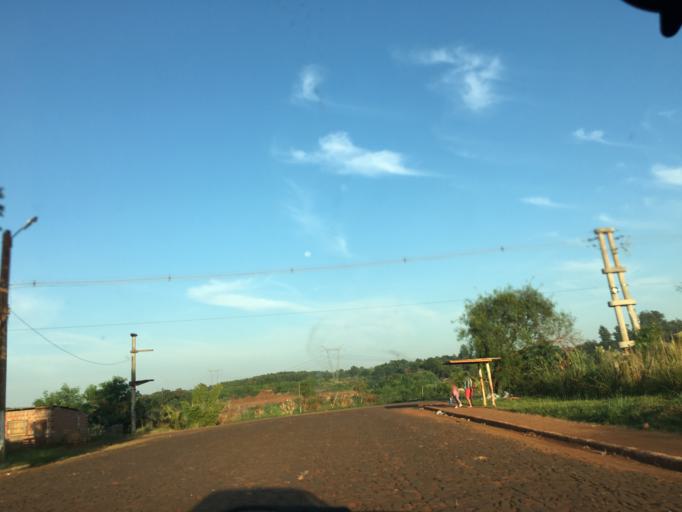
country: AR
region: Misiones
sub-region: Departamento de Capital
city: Posadas
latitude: -27.4524
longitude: -55.9338
